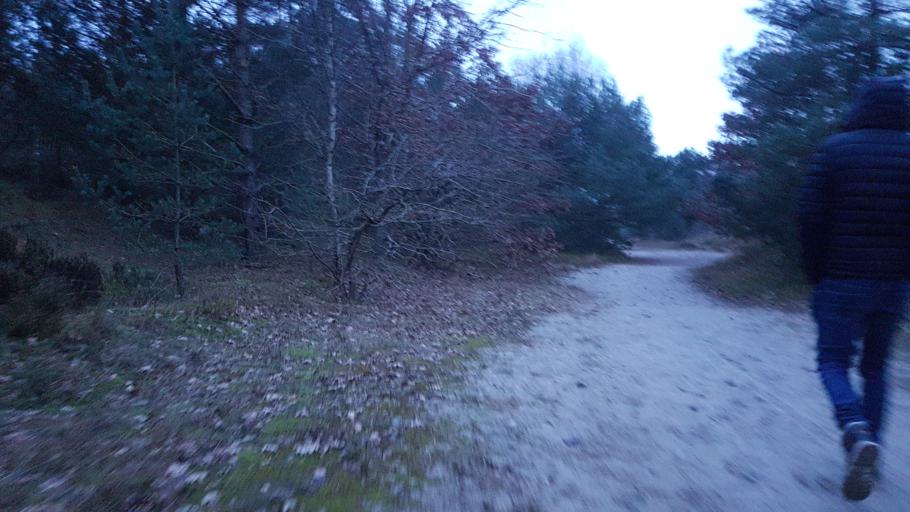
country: DE
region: Mecklenburg-Vorpommern
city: Ostseebad Binz
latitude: 54.4422
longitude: 13.5742
